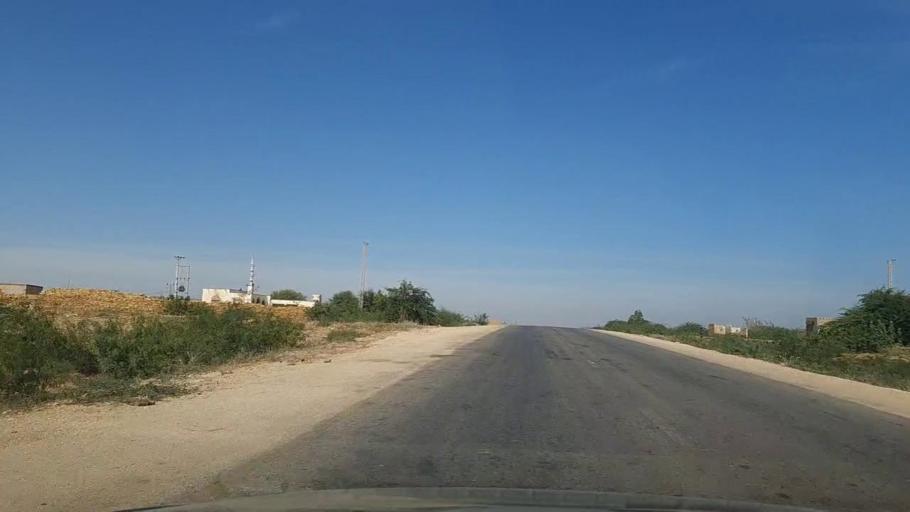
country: PK
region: Sindh
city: Kotri
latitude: 25.1840
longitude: 68.2401
